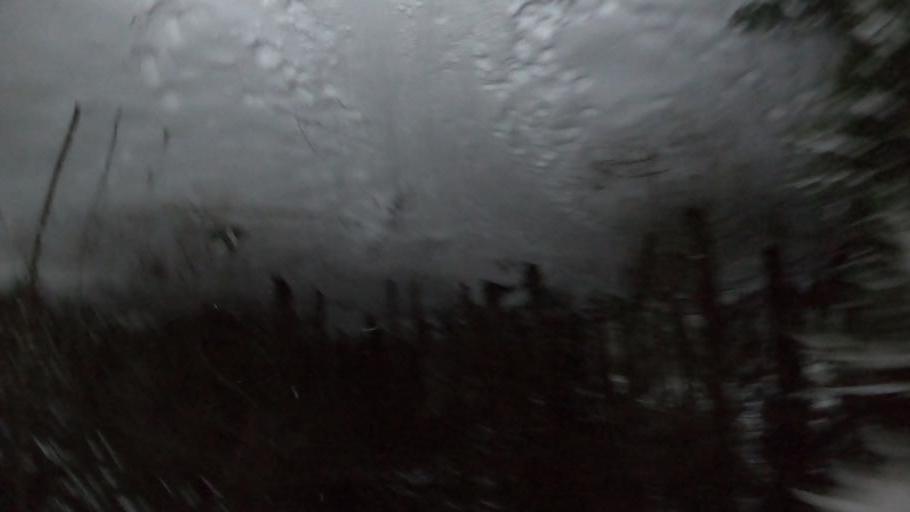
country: RU
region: Moskovskaya
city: Nakhabino
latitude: 55.8913
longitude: 37.2119
